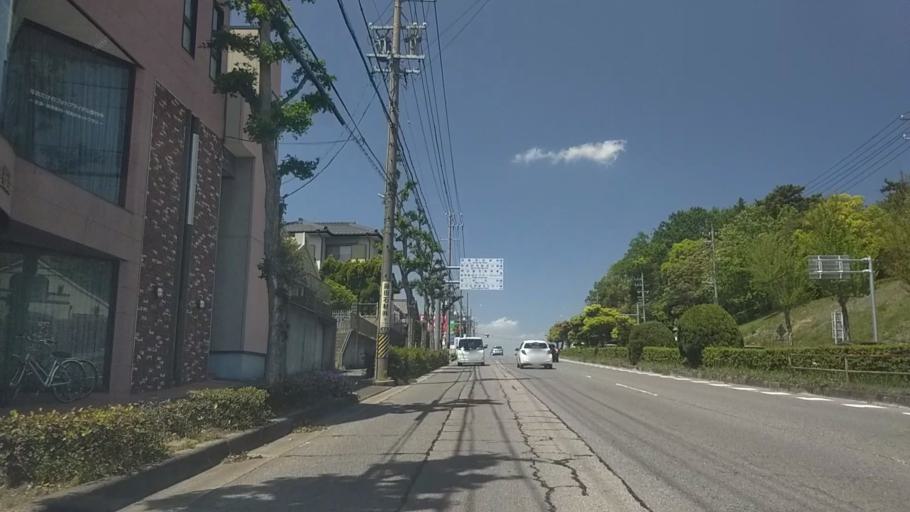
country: JP
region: Aichi
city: Okazaki
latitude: 34.9526
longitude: 137.1898
